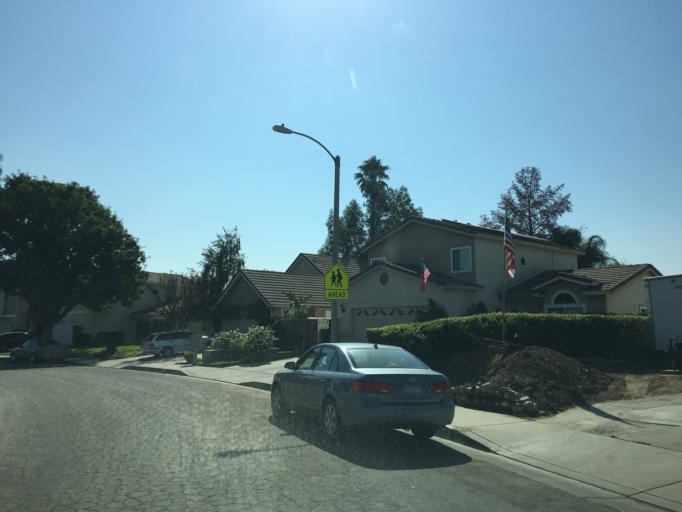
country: US
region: California
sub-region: Los Angeles County
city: Valencia
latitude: 34.4499
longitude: -118.6199
